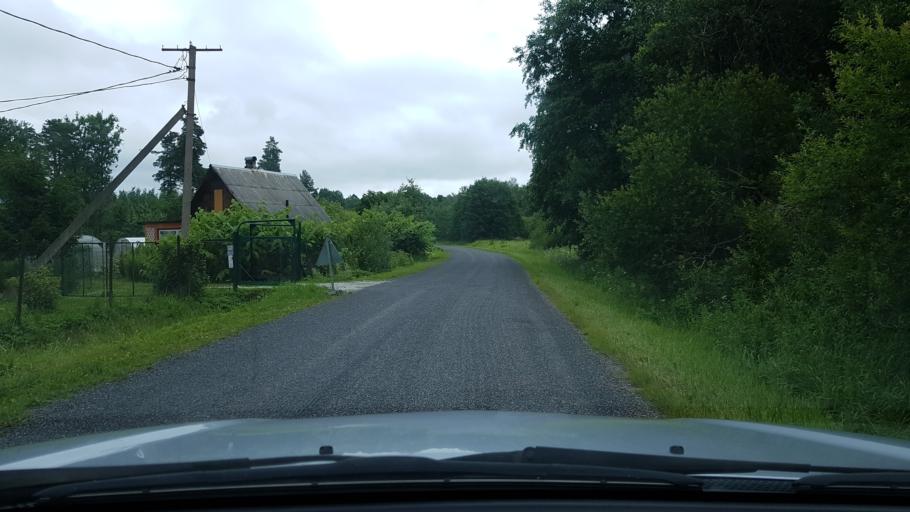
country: EE
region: Ida-Virumaa
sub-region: Narva-Joesuu linn
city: Narva-Joesuu
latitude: 59.3523
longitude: 28.0329
